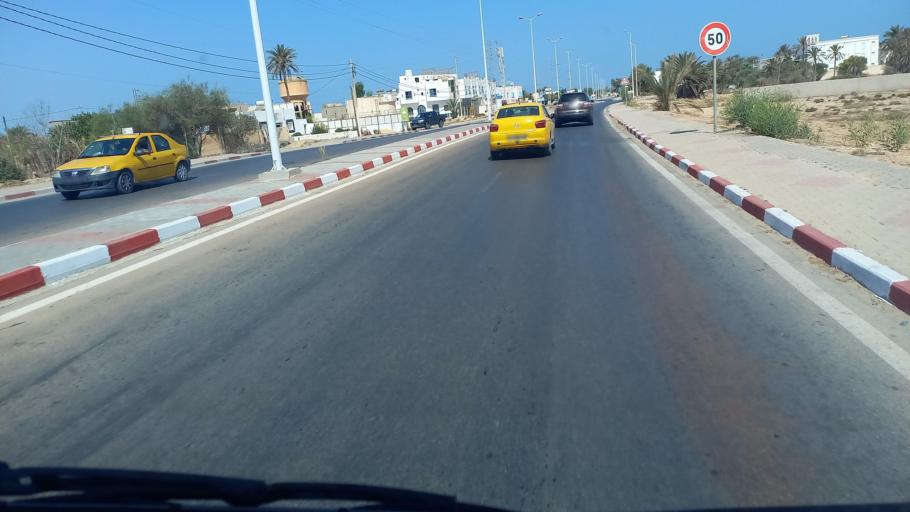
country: TN
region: Madanin
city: Midoun
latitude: 33.8631
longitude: 10.9633
